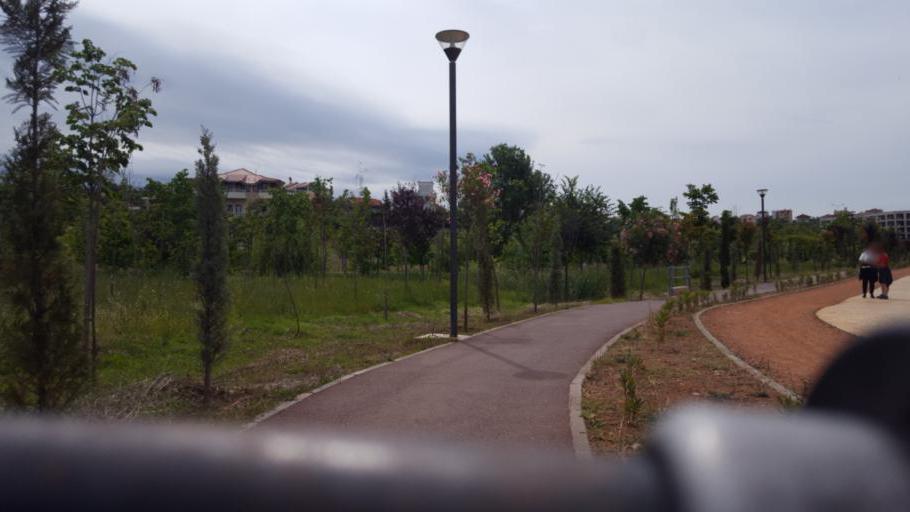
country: AL
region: Tirane
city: Tirana
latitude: 41.3061
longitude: 19.8238
